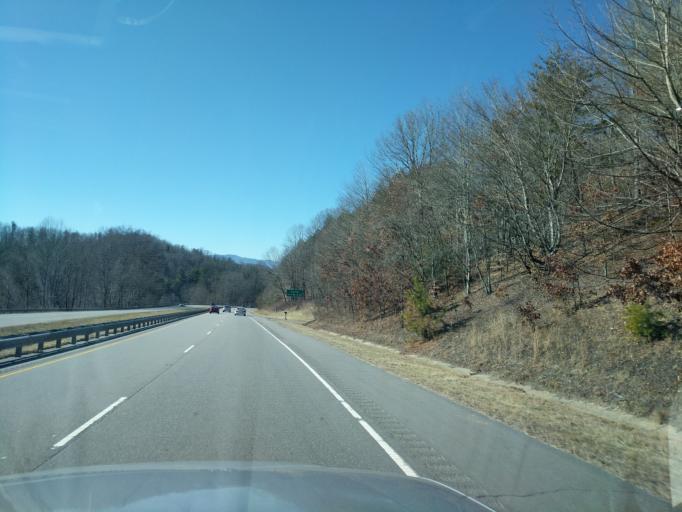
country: US
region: North Carolina
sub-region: Jackson County
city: Sylva
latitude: 35.3943
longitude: -83.1667
